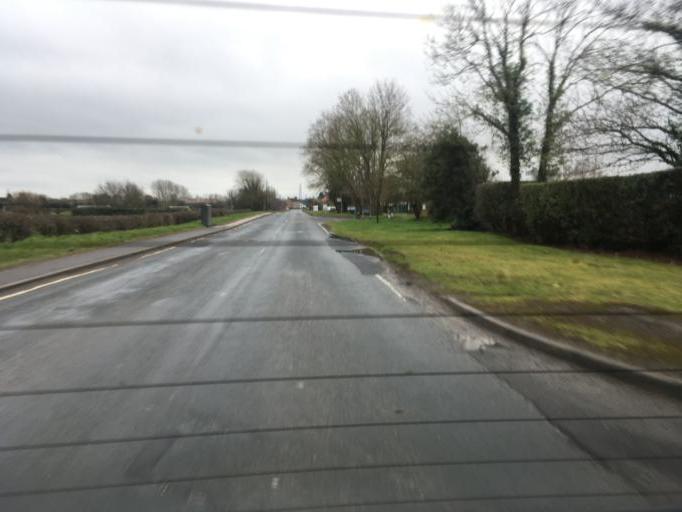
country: GB
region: England
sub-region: City of York
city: Holtby
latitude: 53.9581
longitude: -0.9734
